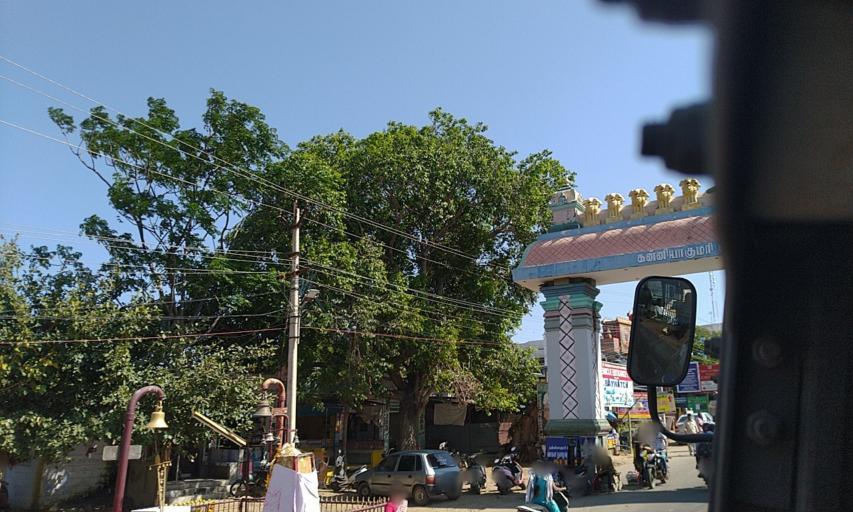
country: IN
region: Tamil Nadu
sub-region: Kanniyakumari
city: Kanniyakumari
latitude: 8.0928
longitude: 77.5492
